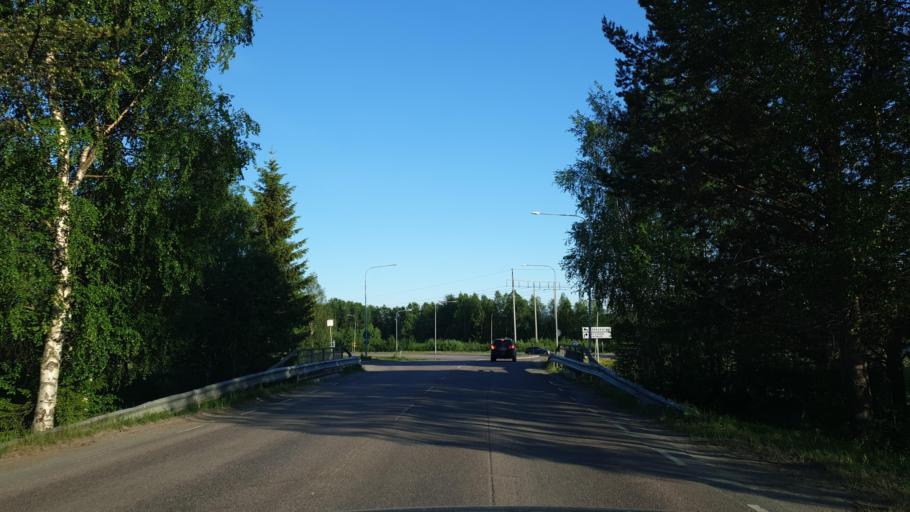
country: SE
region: Norrbotten
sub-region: Lulea Kommun
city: Lulea
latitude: 65.6162
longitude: 22.1479
